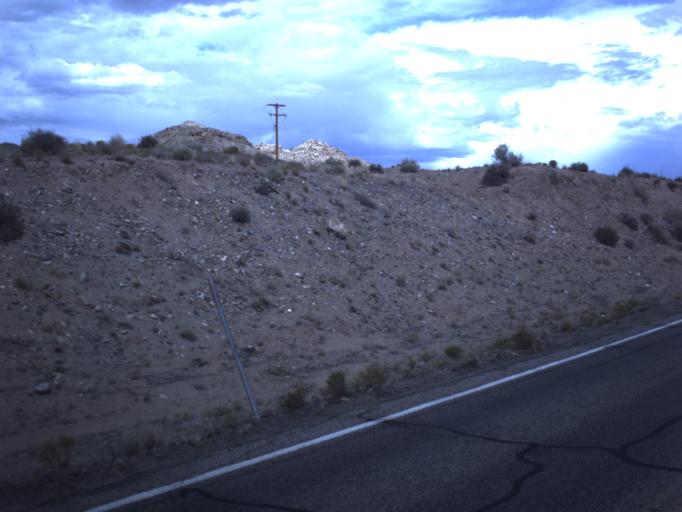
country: US
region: Utah
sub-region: San Juan County
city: Blanding
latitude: 37.2385
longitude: -109.2362
